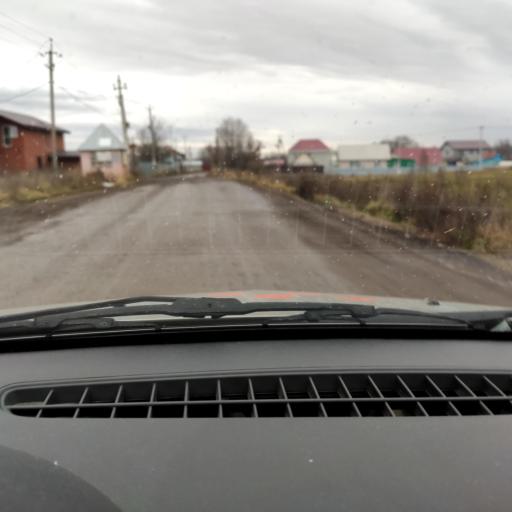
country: RU
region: Bashkortostan
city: Mikhaylovka
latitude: 54.8336
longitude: 55.9461
